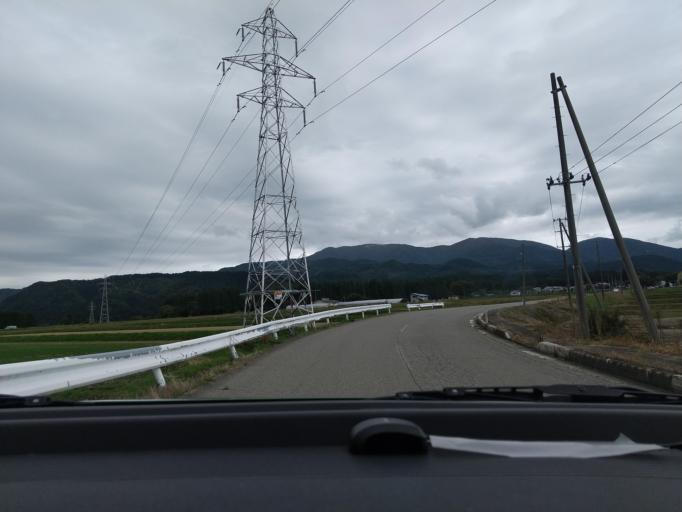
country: JP
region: Akita
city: Kakunodatemachi
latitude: 39.5892
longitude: 140.6039
